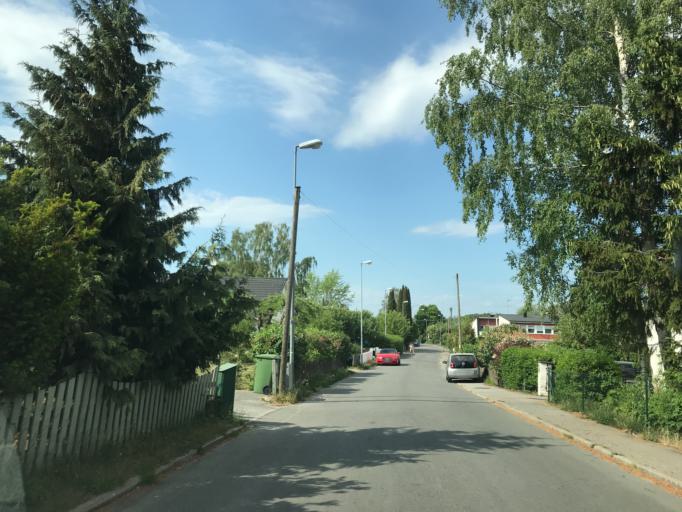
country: SE
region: Stockholm
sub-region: Sollentuna Kommun
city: Sollentuna
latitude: 59.4179
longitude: 17.9575
